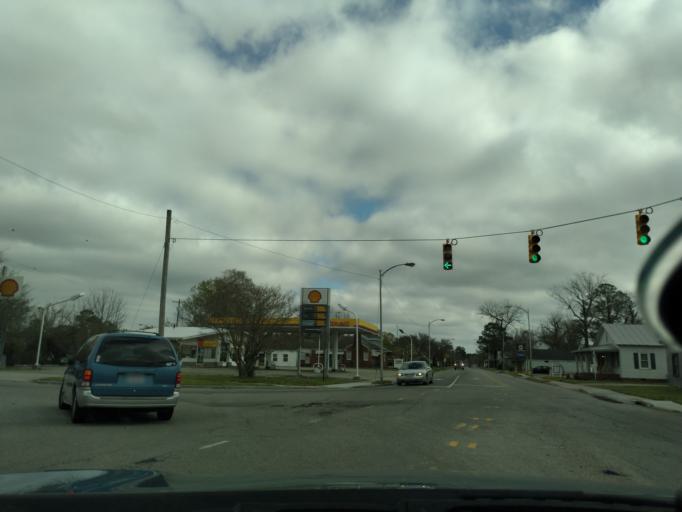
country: US
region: North Carolina
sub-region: Chowan County
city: Edenton
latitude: 36.0694
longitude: -76.6054
